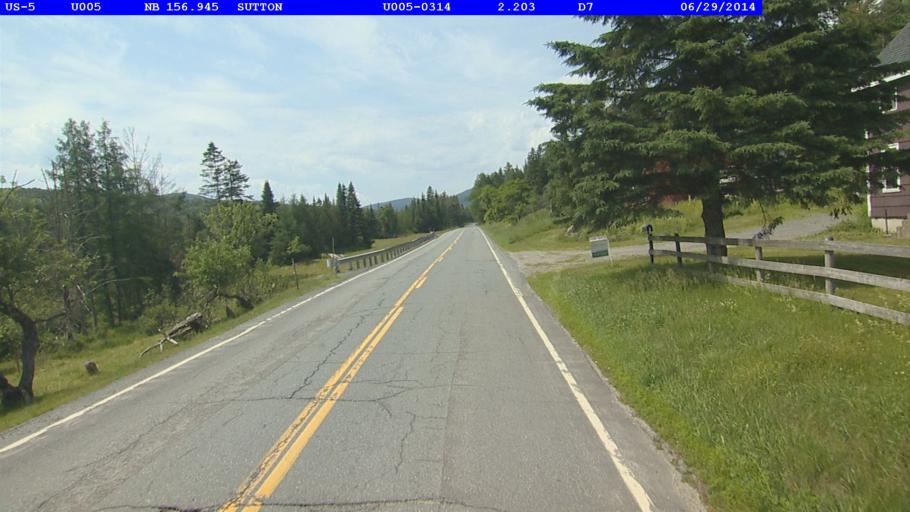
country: US
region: Vermont
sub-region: Caledonia County
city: Lyndonville
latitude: 44.6593
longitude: -72.0194
